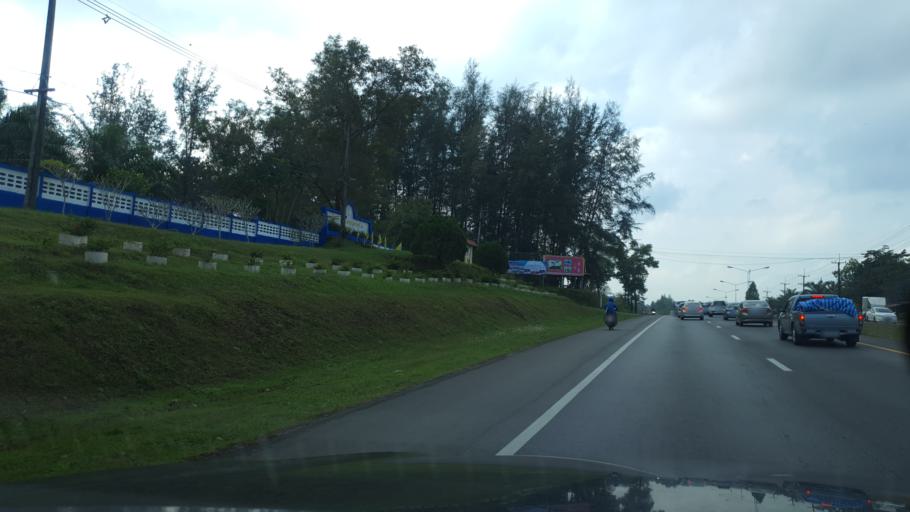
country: TH
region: Chumphon
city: Tha Sae
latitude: 10.8094
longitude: 99.2077
